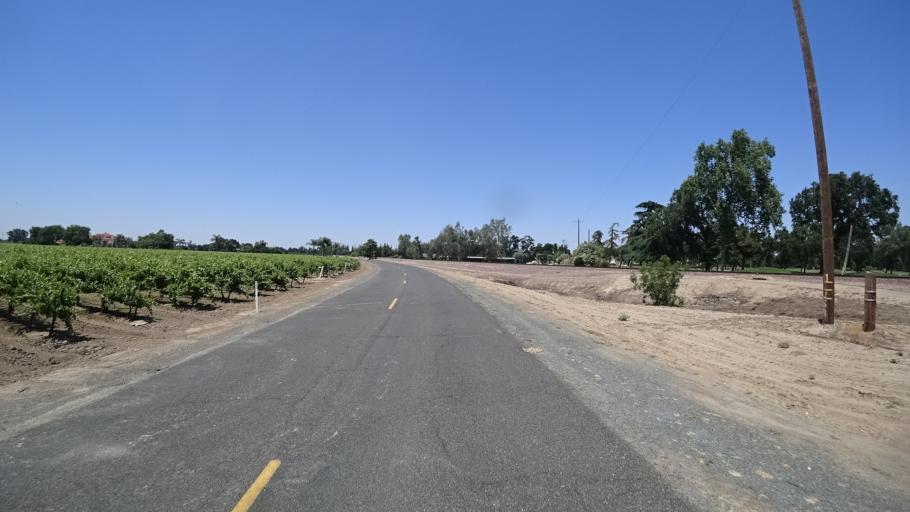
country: US
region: California
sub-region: Fresno County
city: Laton
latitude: 36.4200
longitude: -119.6729
